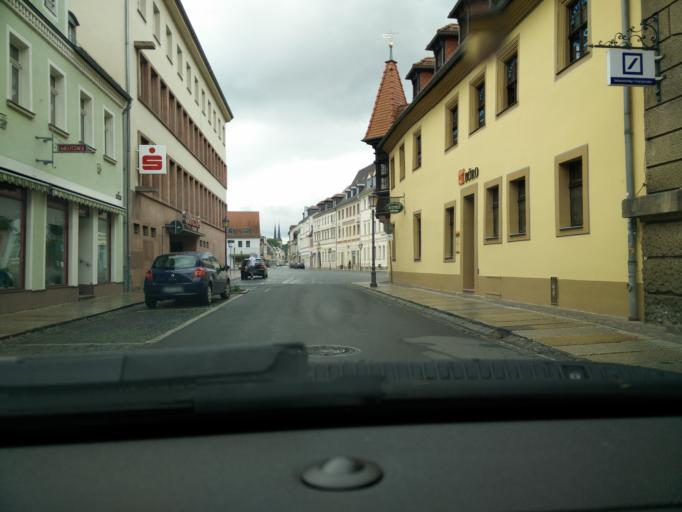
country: DE
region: Saxony
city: Grimma
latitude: 51.2374
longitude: 12.7291
